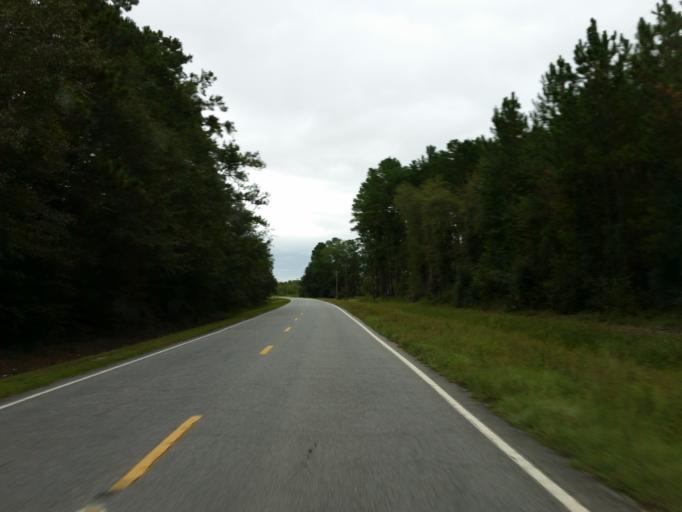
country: US
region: Georgia
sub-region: Echols County
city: Statenville
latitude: 30.8685
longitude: -83.0011
